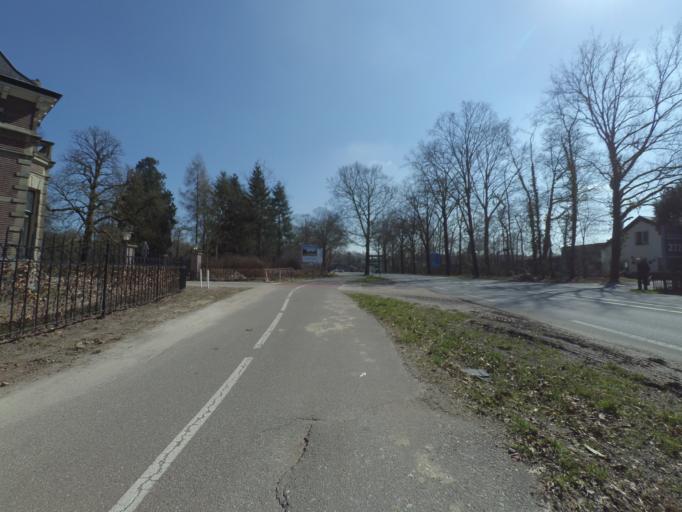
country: NL
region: Utrecht
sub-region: Gemeente Utrechtse Heuvelrug
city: Driebergen-Rijsenburg
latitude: 52.0441
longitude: 5.3015
